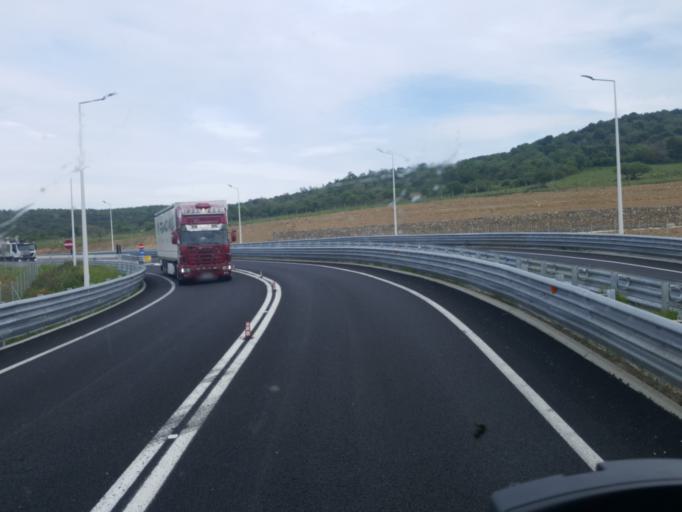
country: IT
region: Latium
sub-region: Provincia di Viterbo
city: Monte Romano
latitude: 42.2820
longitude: 11.9247
